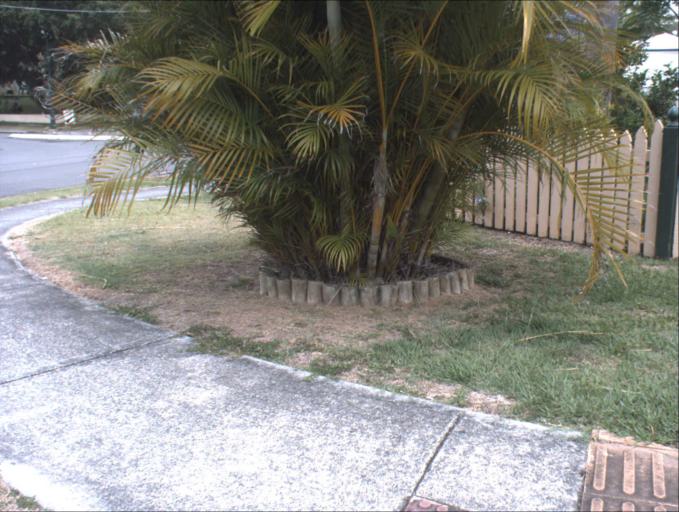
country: AU
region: Queensland
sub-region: Logan
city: Slacks Creek
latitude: -27.6482
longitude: 153.1694
